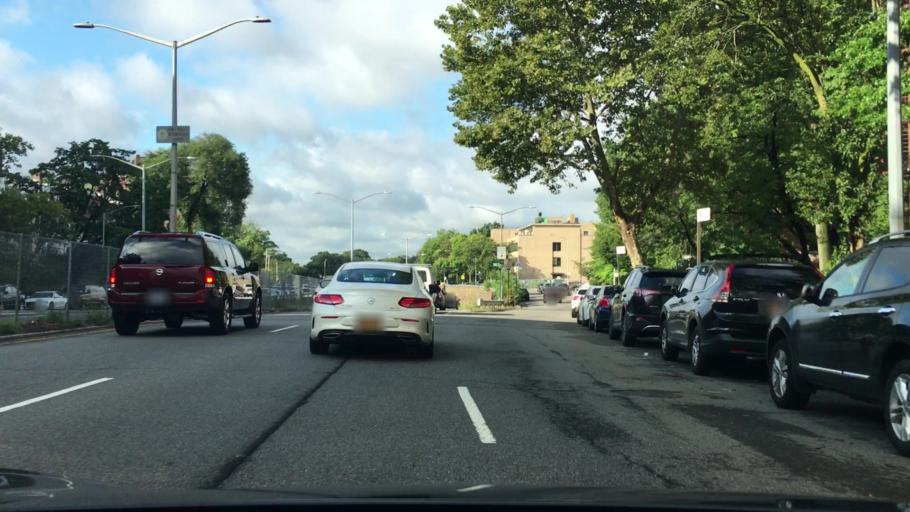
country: US
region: New York
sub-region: Queens County
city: Jamaica
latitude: 40.7124
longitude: -73.8176
